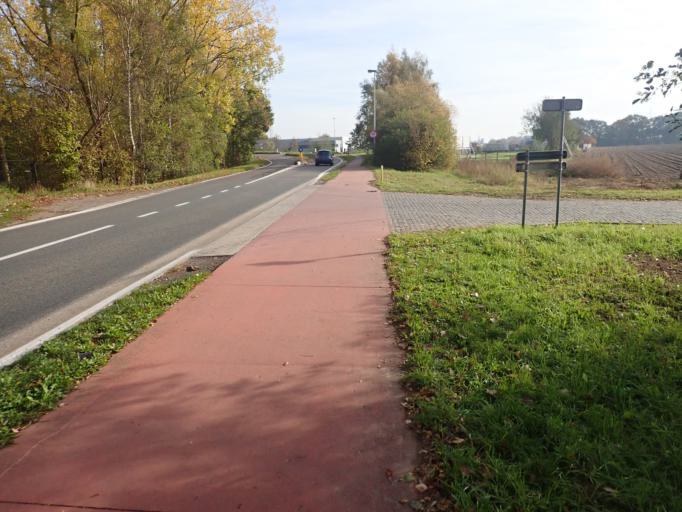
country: BE
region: Flanders
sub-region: Provincie Antwerpen
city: Ranst
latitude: 51.2131
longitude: 4.5724
